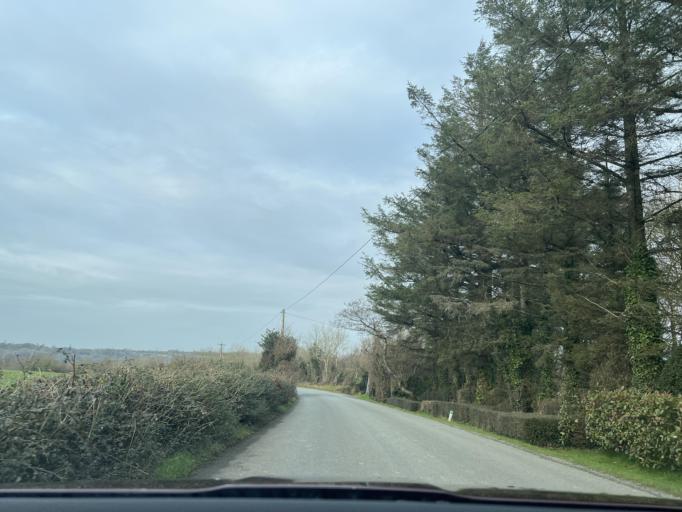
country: IE
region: Leinster
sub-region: Loch Garman
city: Castlebridge
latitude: 52.3805
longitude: -6.5488
